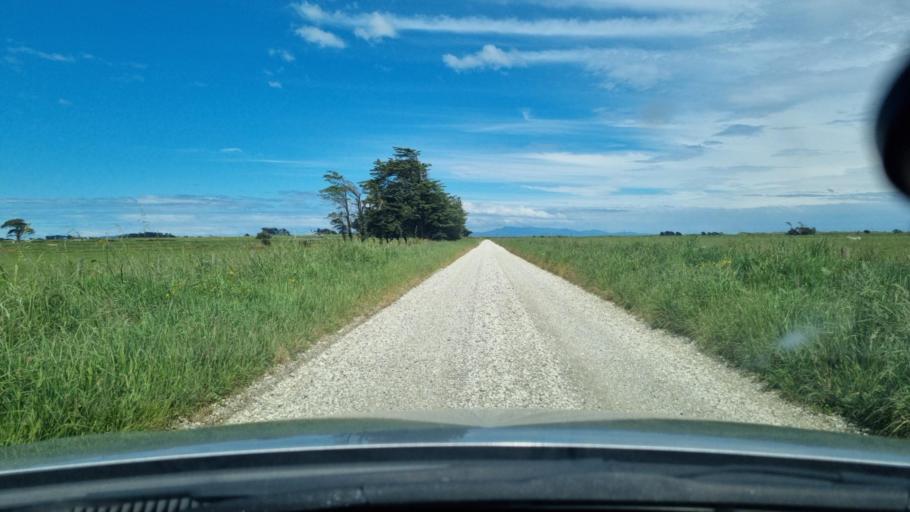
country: NZ
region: Southland
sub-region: Invercargill City
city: Invercargill
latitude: -46.3865
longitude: 168.2642
